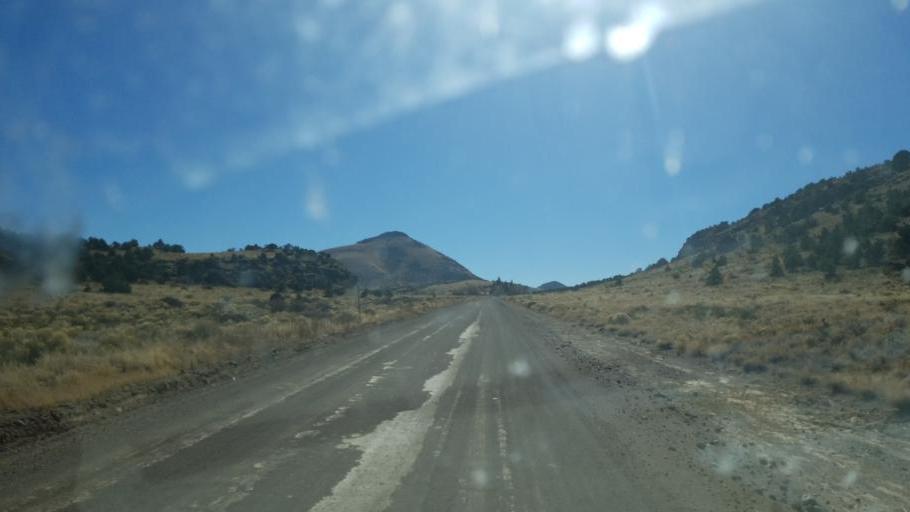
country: US
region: Colorado
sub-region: Rio Grande County
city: Del Norte
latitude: 37.6348
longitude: -106.3655
